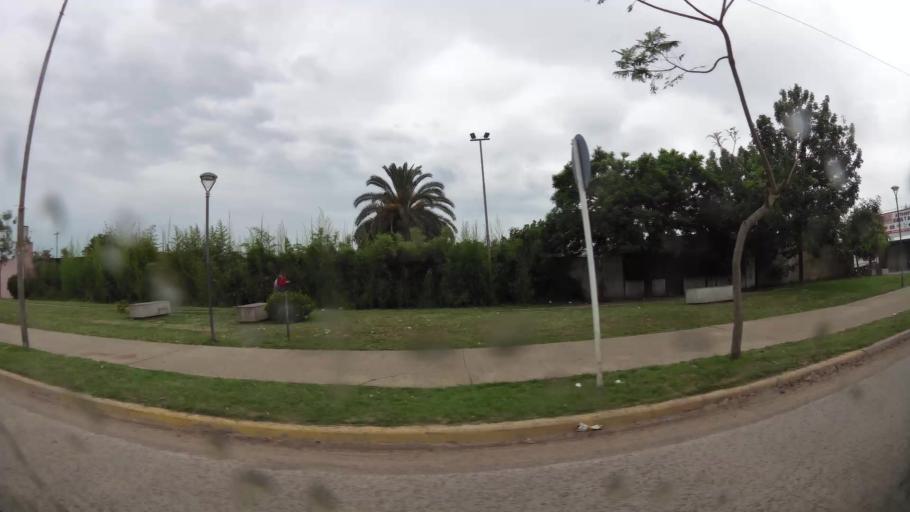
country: AR
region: Buenos Aires
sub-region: Partido de Zarate
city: Zarate
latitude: -34.1102
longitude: -59.0334
